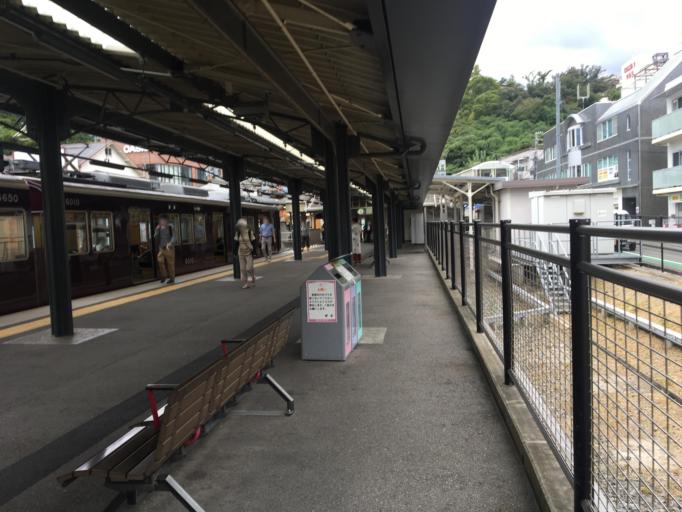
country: JP
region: Hyogo
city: Ashiya
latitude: 34.7608
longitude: 135.3305
